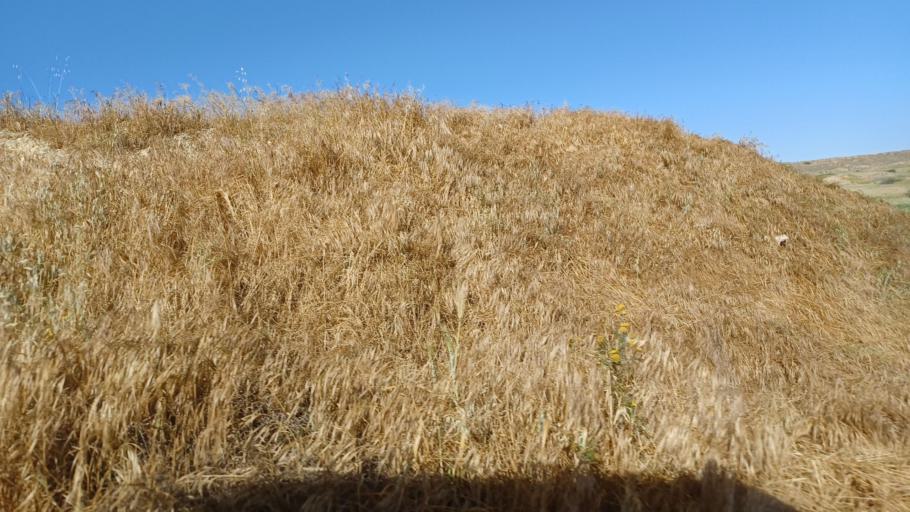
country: CY
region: Lefkosia
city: Mammari
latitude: 35.1593
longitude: 33.2430
